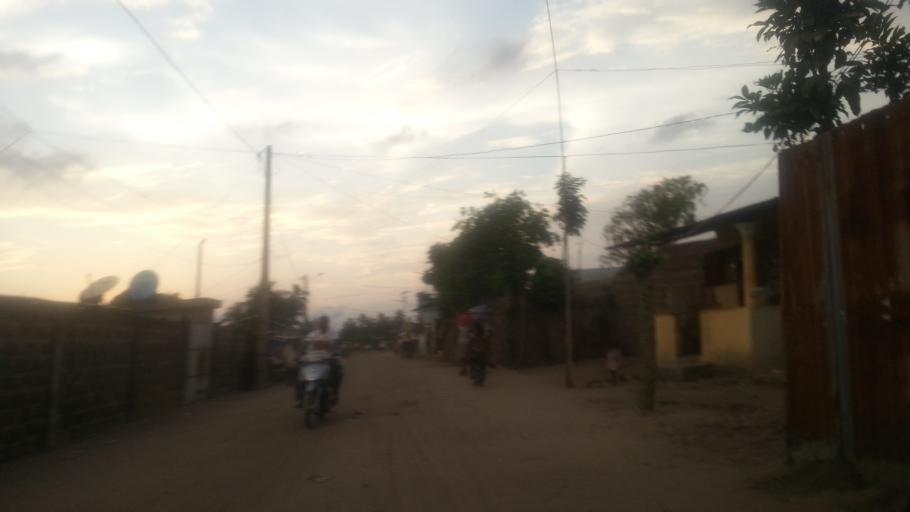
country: BJ
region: Littoral
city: Cotonou
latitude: 6.3876
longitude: 2.5401
